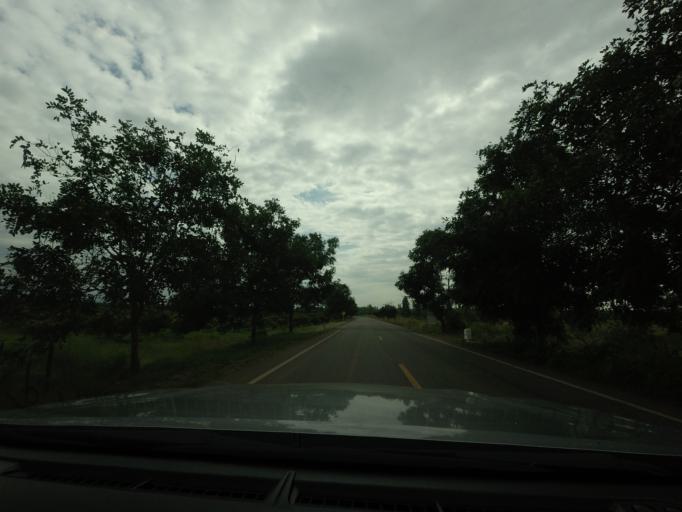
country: TH
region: Phitsanulok
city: Noen Maprang
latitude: 16.6105
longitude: 100.6200
